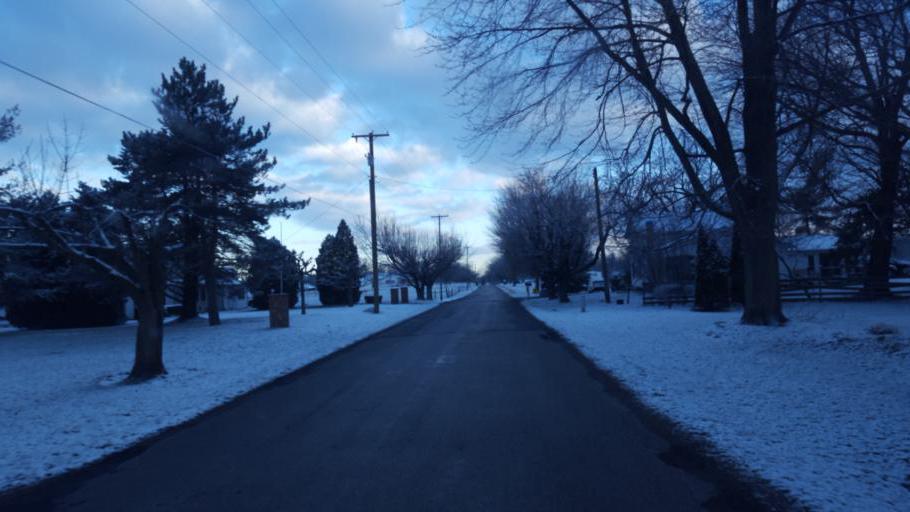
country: US
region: Ohio
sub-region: Morrow County
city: Mount Gilead
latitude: 40.5592
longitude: -82.8388
